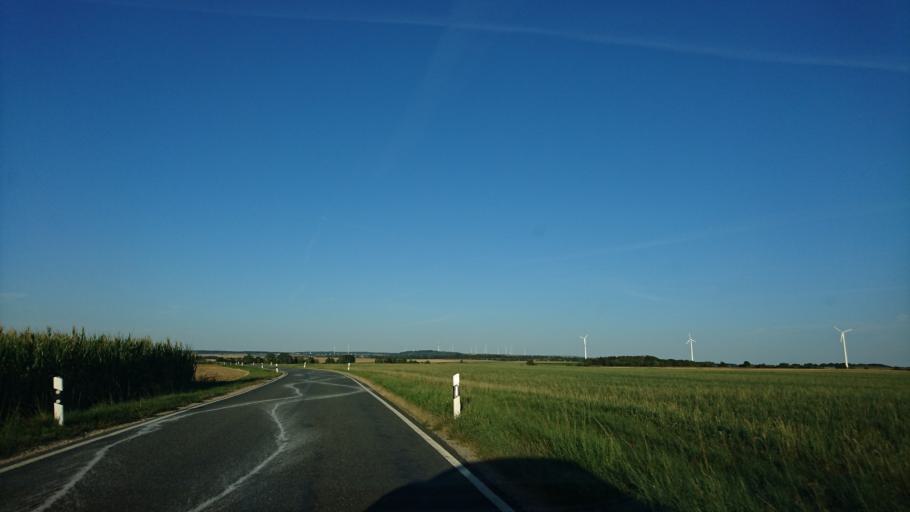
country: DE
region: Bavaria
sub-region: Regierungsbezirk Mittelfranken
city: Thalmassing
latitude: 49.0658
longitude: 11.1834
